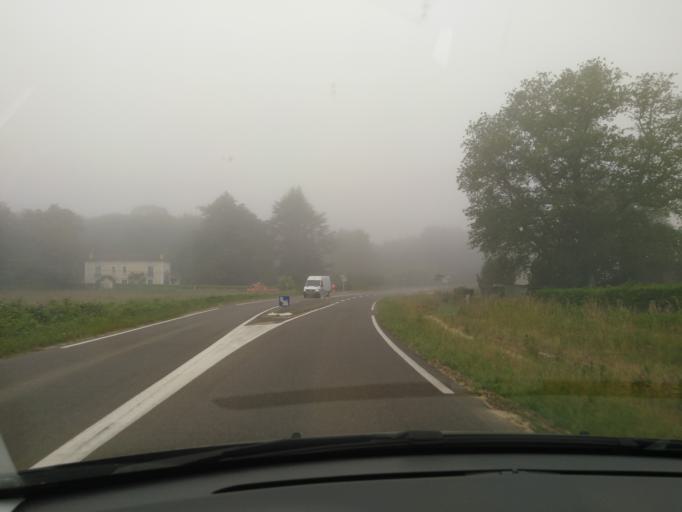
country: FR
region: Aquitaine
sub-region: Departement des Landes
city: Villeneuve-de-Marsan
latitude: 43.8824
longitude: -0.3482
